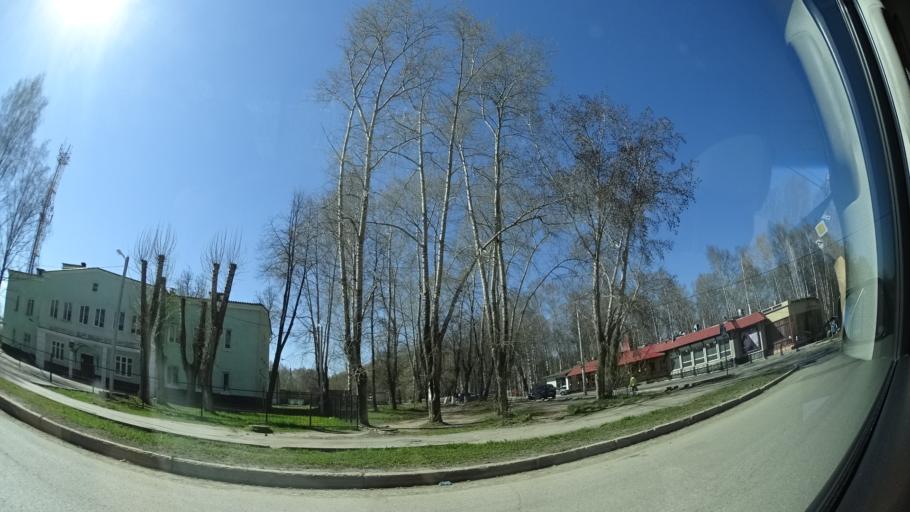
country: RU
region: Perm
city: Perm
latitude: 58.1117
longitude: 56.3038
